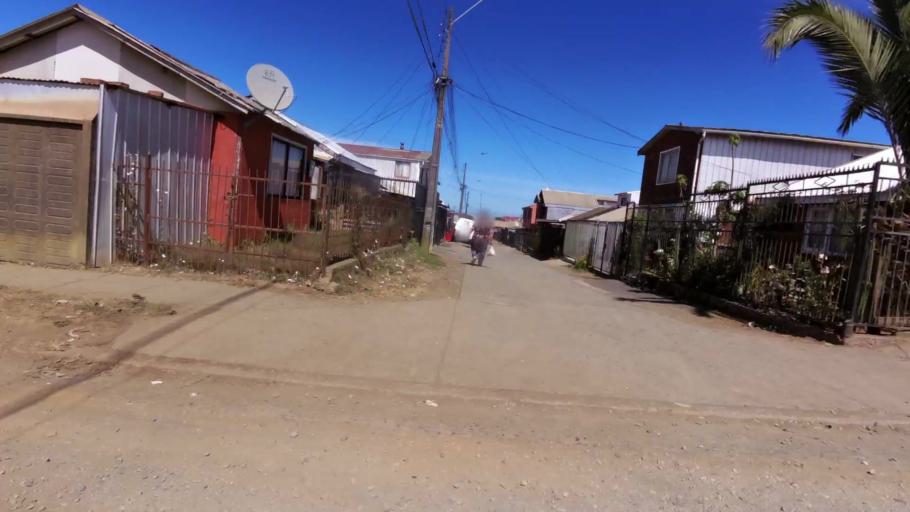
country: CL
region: Biobio
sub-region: Provincia de Concepcion
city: Talcahuano
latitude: -36.7122
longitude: -73.1330
